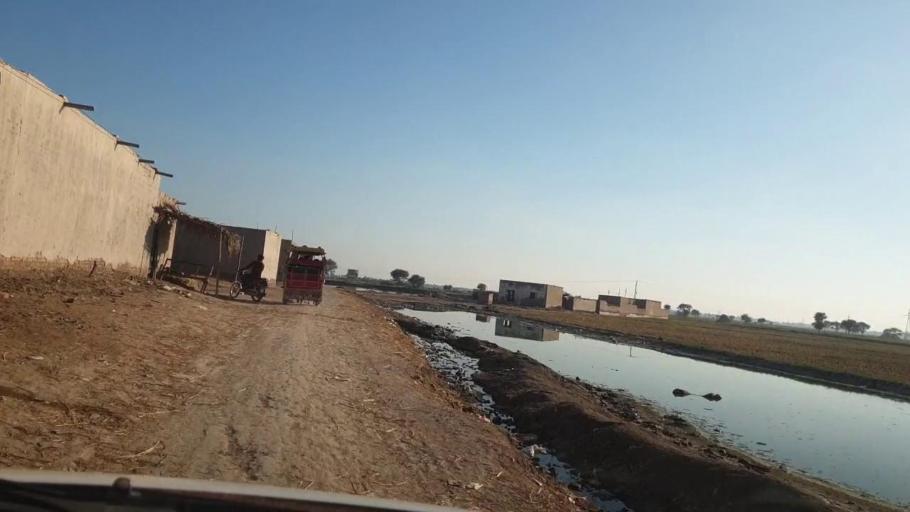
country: PK
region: Sindh
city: Khairpur Nathan Shah
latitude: 27.0476
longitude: 67.7246
